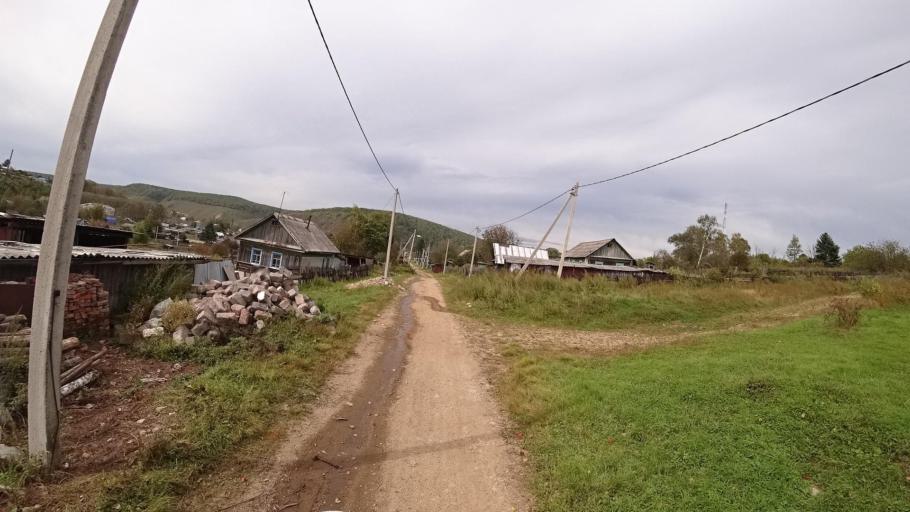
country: RU
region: Jewish Autonomous Oblast
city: Khingansk
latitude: 49.1234
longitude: 131.2068
